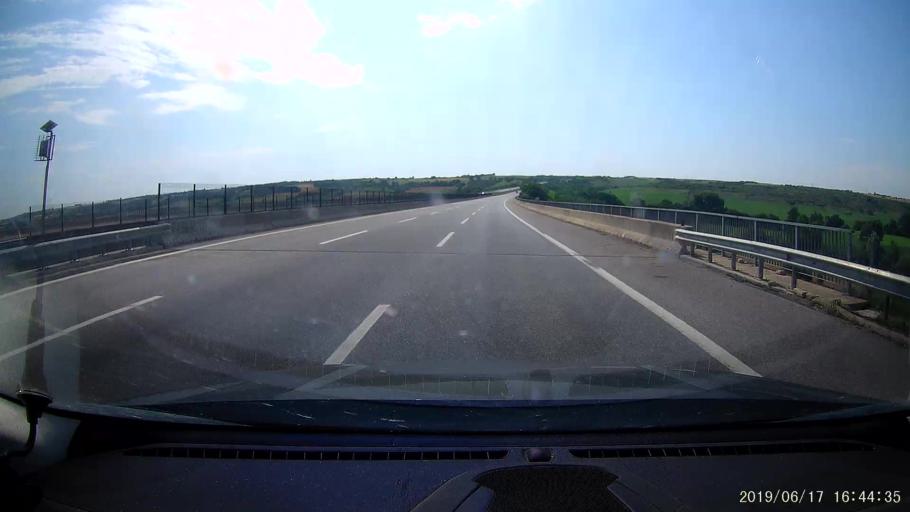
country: TR
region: Kirklareli
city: Luleburgaz
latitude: 41.4820
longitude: 27.2563
